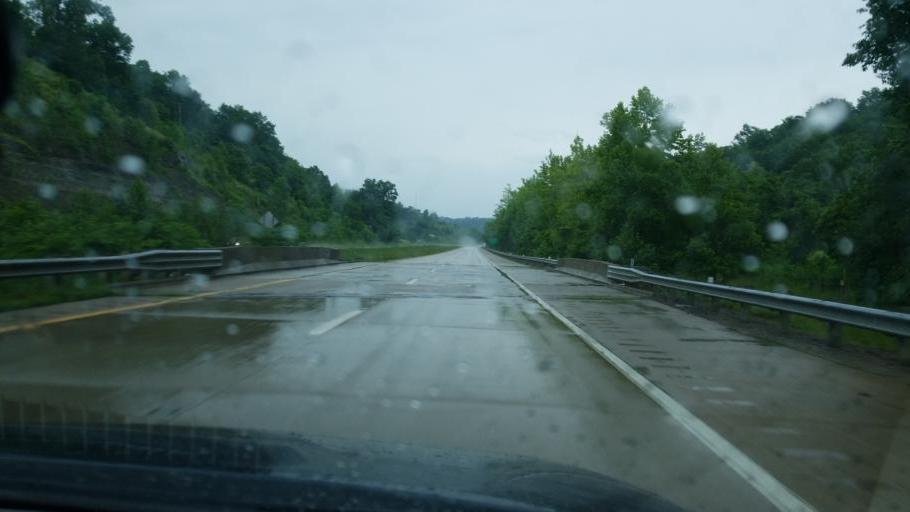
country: US
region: Ohio
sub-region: Athens County
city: Athens
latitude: 39.2751
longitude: -81.9290
